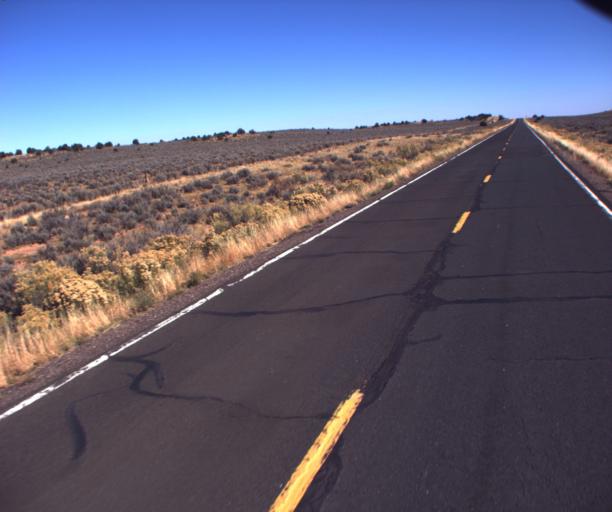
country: US
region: Arizona
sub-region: Navajo County
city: First Mesa
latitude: 35.7481
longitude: -110.0498
